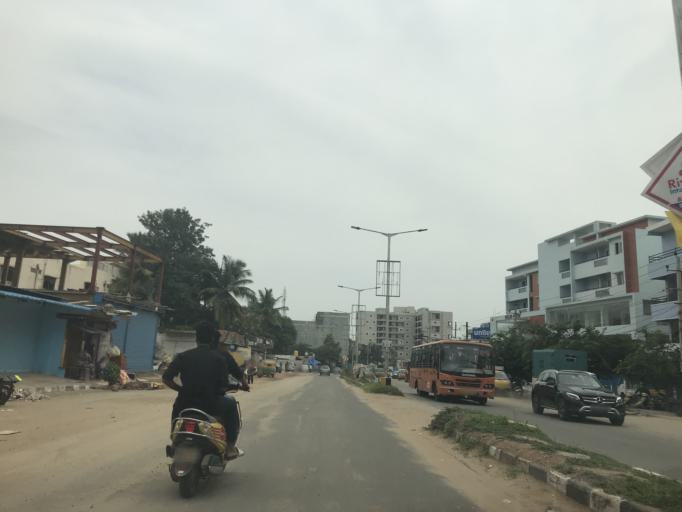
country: IN
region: Karnataka
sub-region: Bangalore Urban
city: Yelahanka
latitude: 13.0590
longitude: 77.6487
